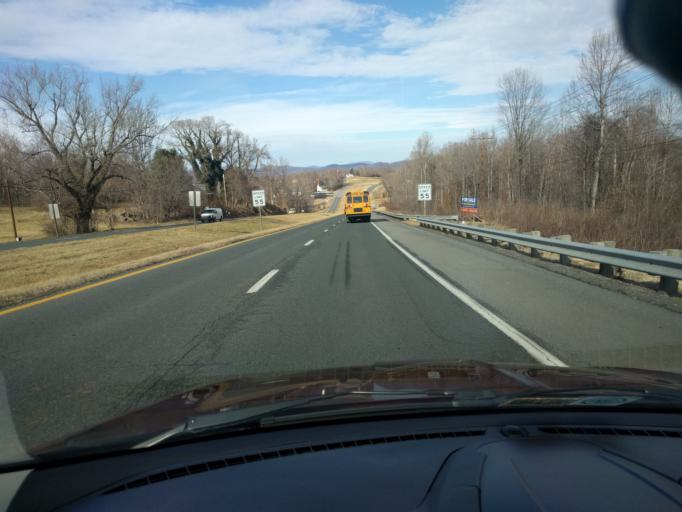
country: US
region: Virginia
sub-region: Amherst County
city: Madison Heights
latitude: 37.4953
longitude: -79.1254
